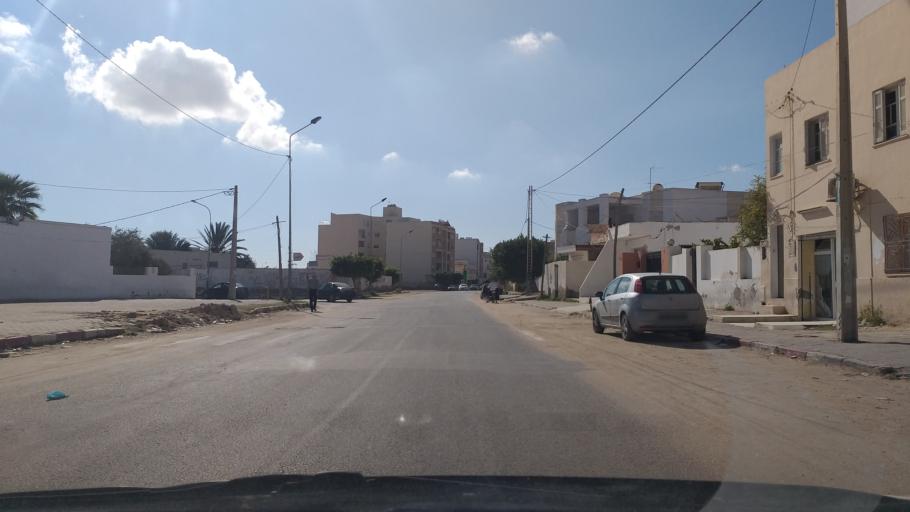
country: TN
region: Safaqis
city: Al Qarmadah
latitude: 34.7996
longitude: 10.7814
